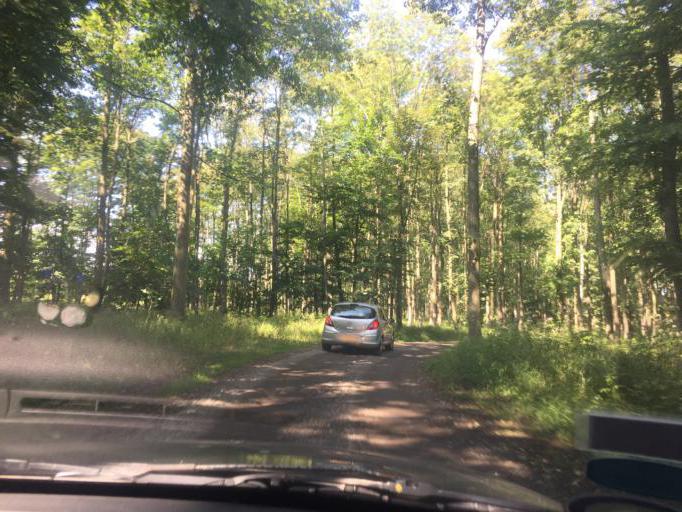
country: DK
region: Zealand
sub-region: Lolland Kommune
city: Maribo
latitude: 54.8169
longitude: 11.5011
